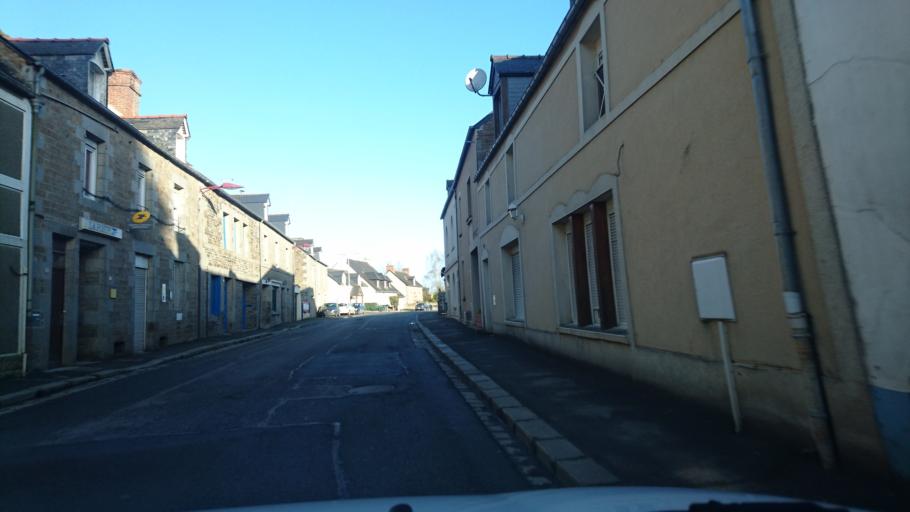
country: FR
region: Brittany
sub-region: Departement d'Ille-et-Vilaine
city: La Boussac
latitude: 48.5129
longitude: -1.6617
